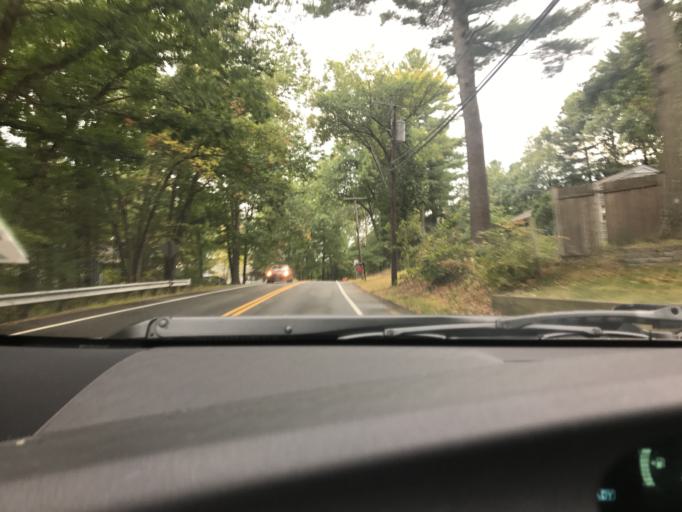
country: US
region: Massachusetts
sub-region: Middlesex County
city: Littleton Common
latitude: 42.5743
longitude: -71.4749
